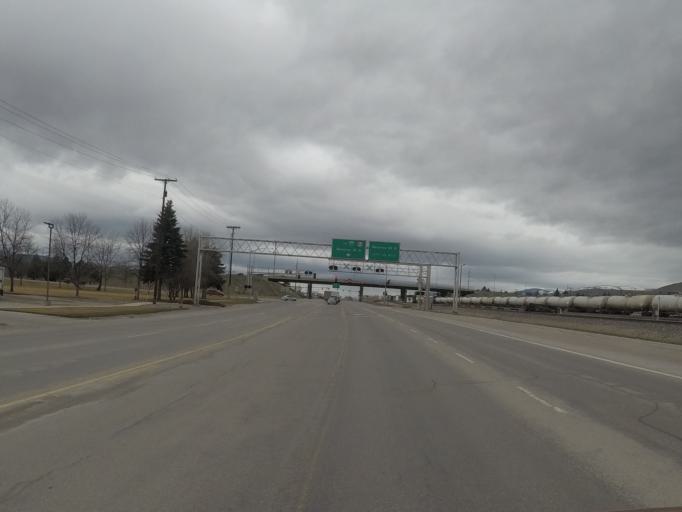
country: US
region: Montana
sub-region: Missoula County
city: Orchard Homes
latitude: 46.8973
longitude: -114.0358
